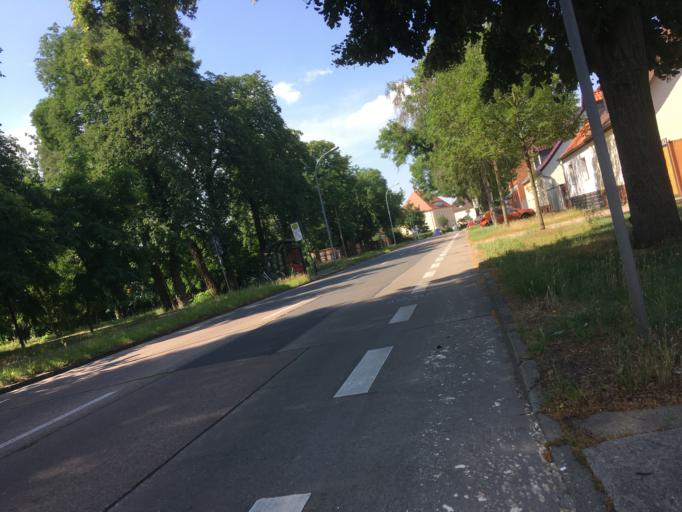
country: DE
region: Saxony-Anhalt
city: Dessau
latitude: 51.7983
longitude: 12.1873
